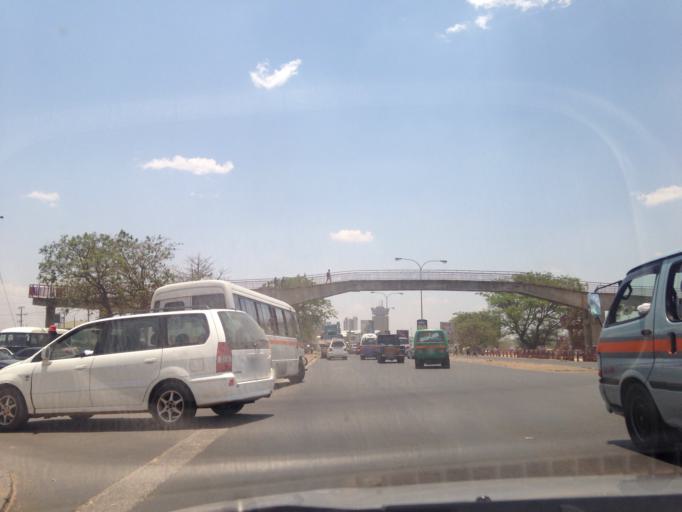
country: ZM
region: Lusaka
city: Lusaka
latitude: -15.4342
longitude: 28.2776
